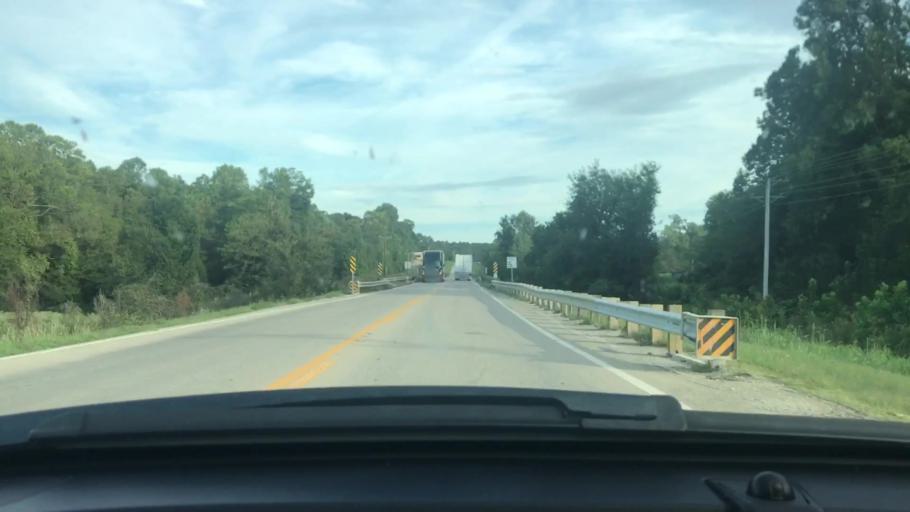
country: US
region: Arkansas
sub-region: Lawrence County
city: Hoxie
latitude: 36.1217
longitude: -91.1495
